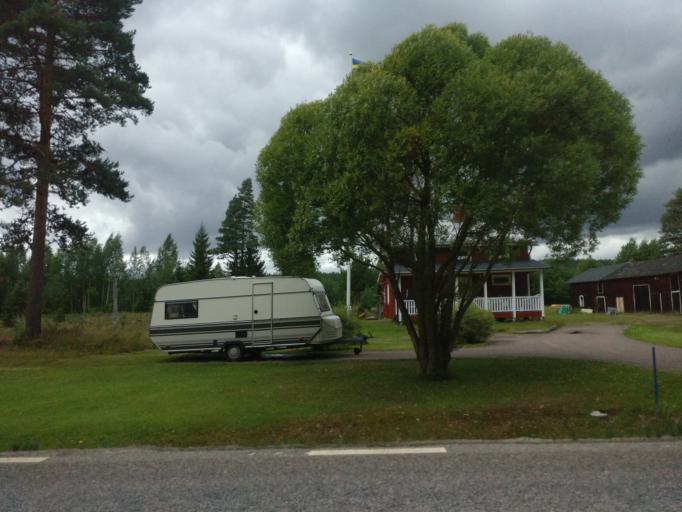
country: SE
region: Vaermland
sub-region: Torsby Kommun
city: Torsby
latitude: 60.7639
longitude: 12.7614
